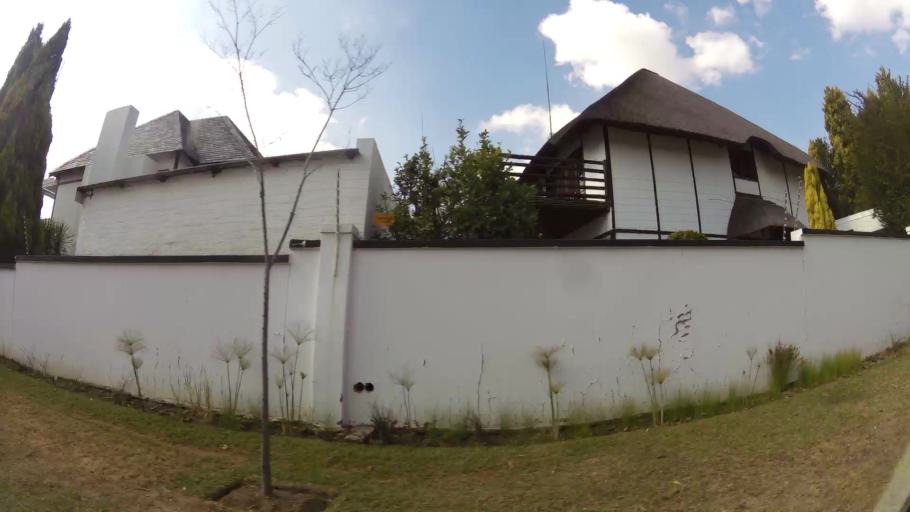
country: ZA
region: Gauteng
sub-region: City of Johannesburg Metropolitan Municipality
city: Midrand
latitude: -26.0239
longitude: 28.0752
